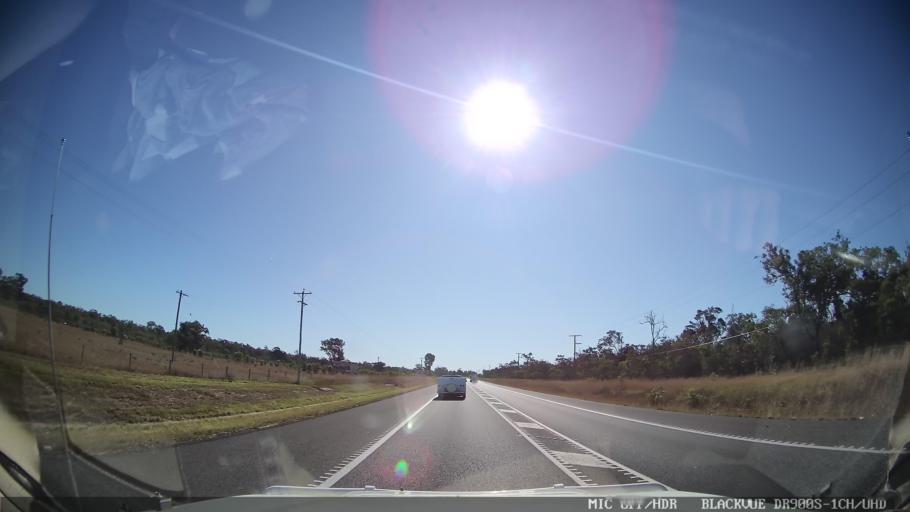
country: AU
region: Queensland
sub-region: Bundaberg
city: Childers
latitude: -25.2777
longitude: 152.3846
